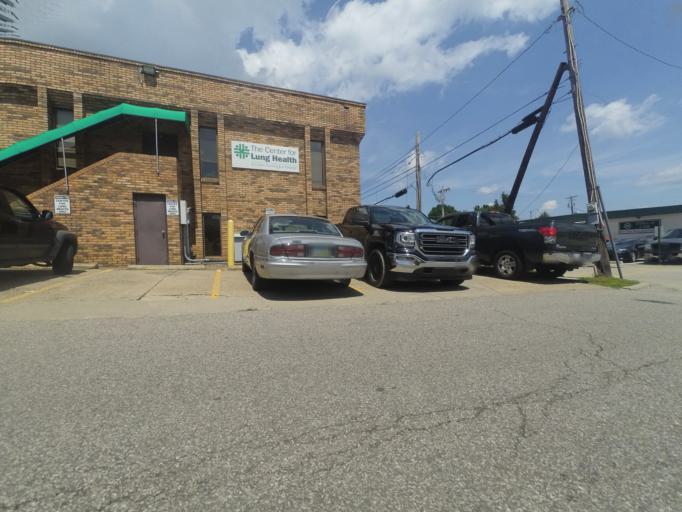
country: US
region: West Virginia
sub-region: Cabell County
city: Huntington
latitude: 38.4105
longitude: -82.4268
